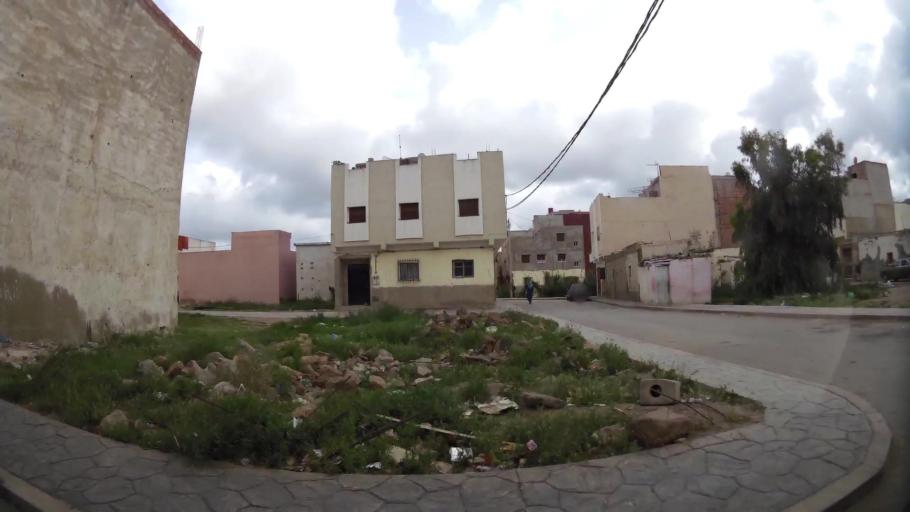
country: MA
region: Oriental
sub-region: Nador
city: Nador
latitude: 35.1605
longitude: -2.9132
